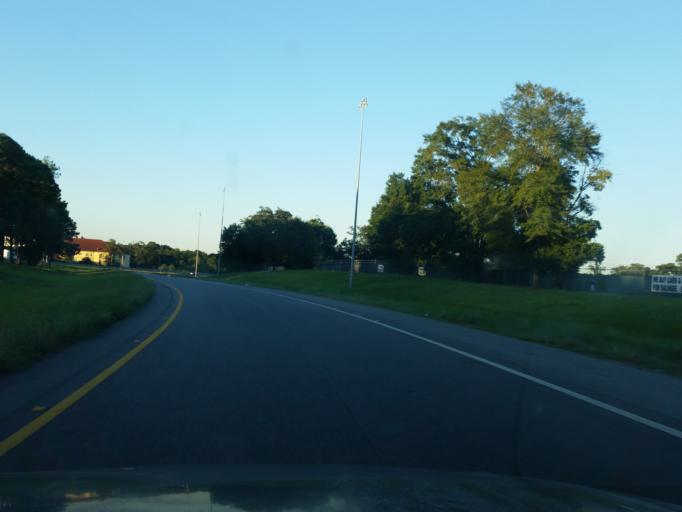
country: US
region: Alabama
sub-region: Mobile County
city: Tillmans Corner
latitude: 30.5802
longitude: -88.1679
